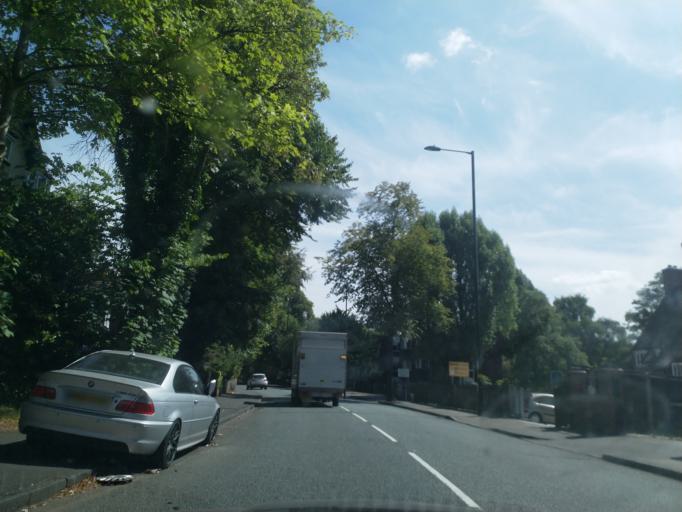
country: GB
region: England
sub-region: City and Borough of Birmingham
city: Hockley
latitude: 52.5129
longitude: -1.9241
